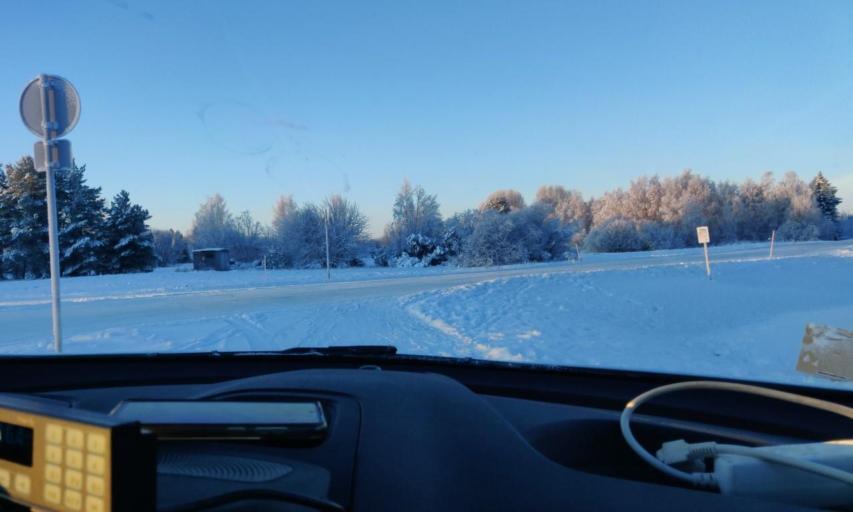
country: FI
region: Northern Ostrobothnia
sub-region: Raahe
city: Siikajoki
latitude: 64.8158
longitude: 24.7670
